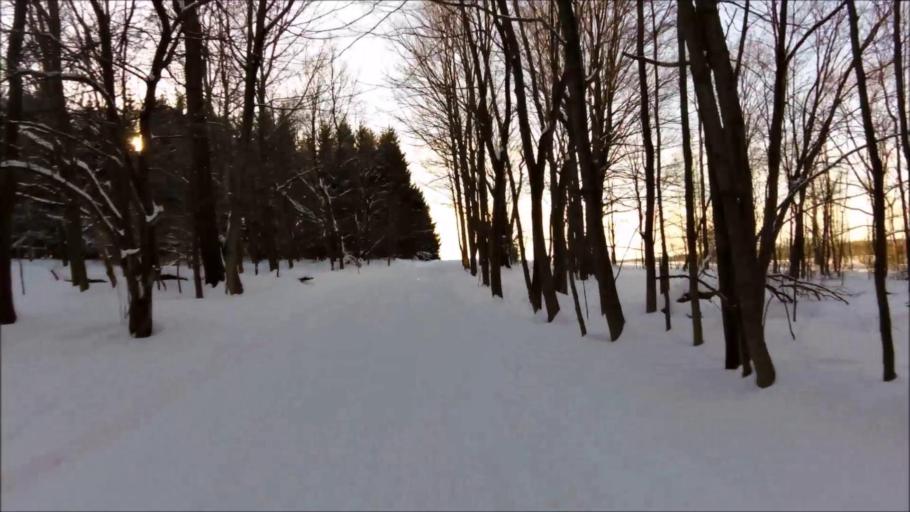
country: US
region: New York
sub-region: Chautauqua County
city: Mayville
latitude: 42.2496
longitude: -79.3880
